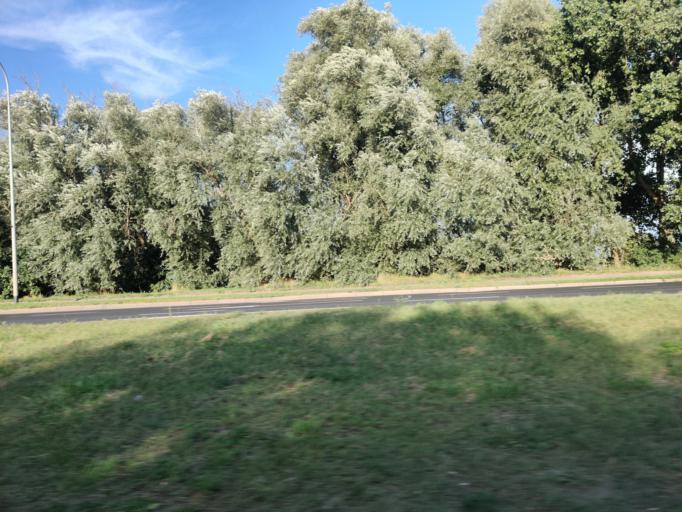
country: PL
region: Greater Poland Voivodeship
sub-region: Konin
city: Konin
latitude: 52.2219
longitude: 18.2514
